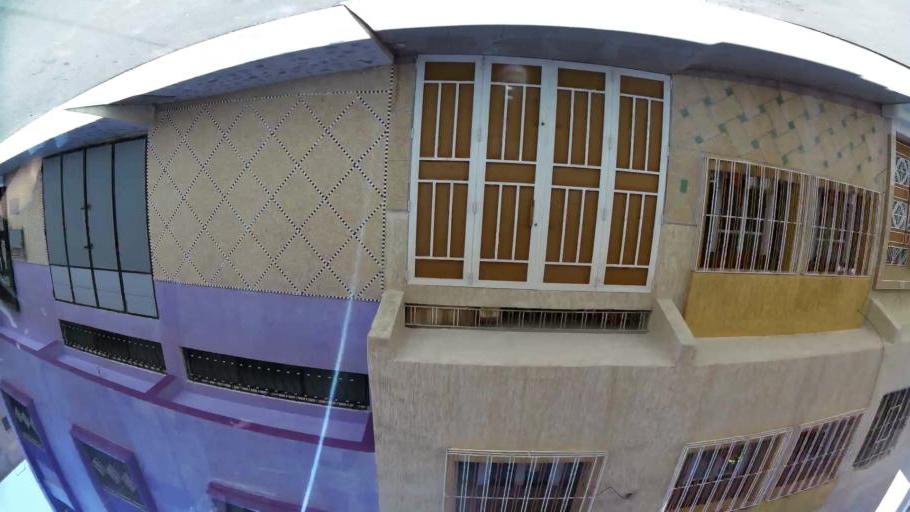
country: MA
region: Meknes-Tafilalet
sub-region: Meknes
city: Meknes
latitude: 33.8978
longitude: -5.5779
